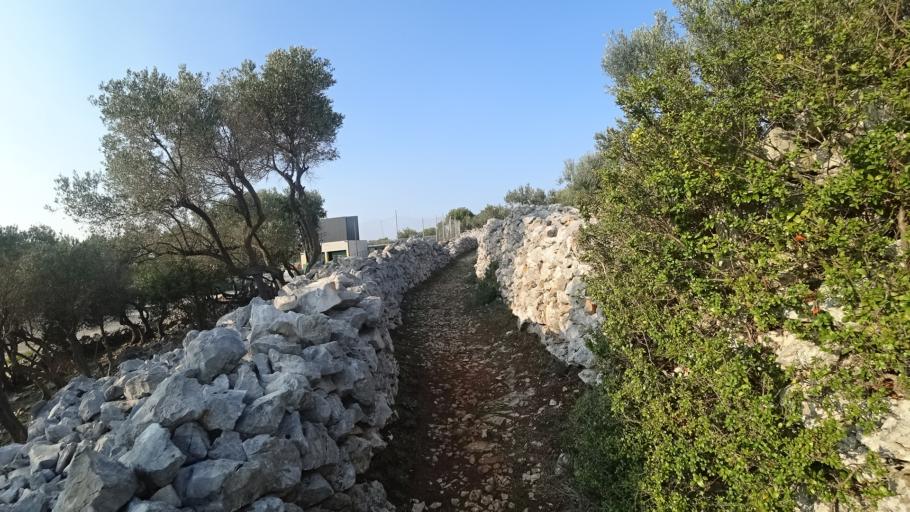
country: HR
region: Primorsko-Goranska
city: Mali Losinj
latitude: 44.5211
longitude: 14.4771
